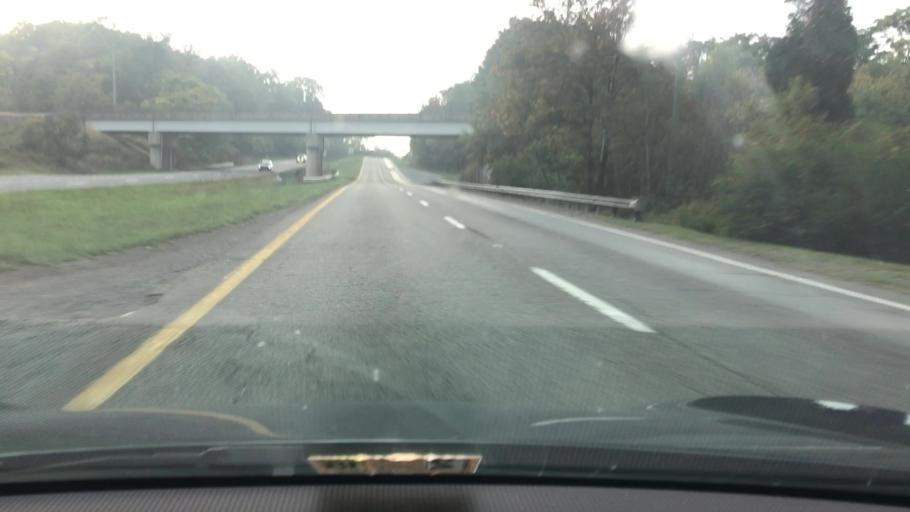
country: US
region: Virginia
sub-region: Botetourt County
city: Blue Ridge
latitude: 37.3950
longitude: -79.7479
